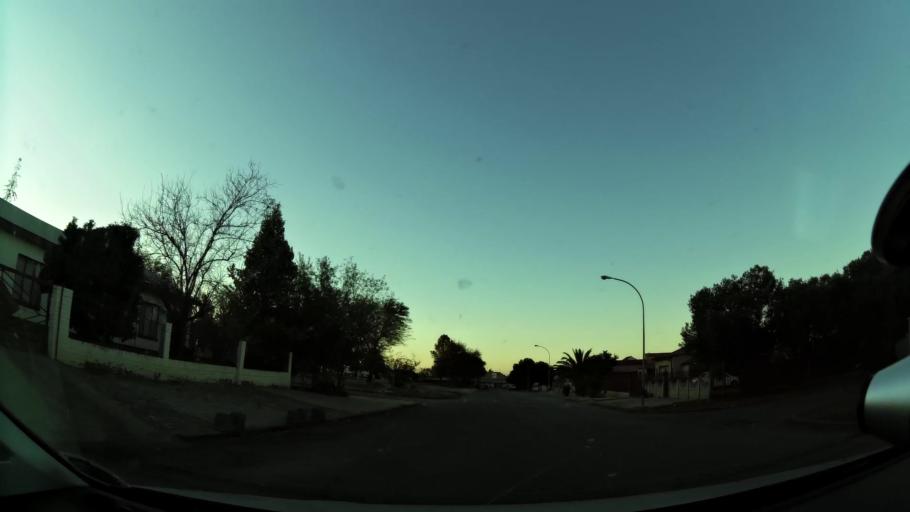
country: ZA
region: Northern Cape
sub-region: Frances Baard District Municipality
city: Kimberley
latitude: -28.7318
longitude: 24.7735
